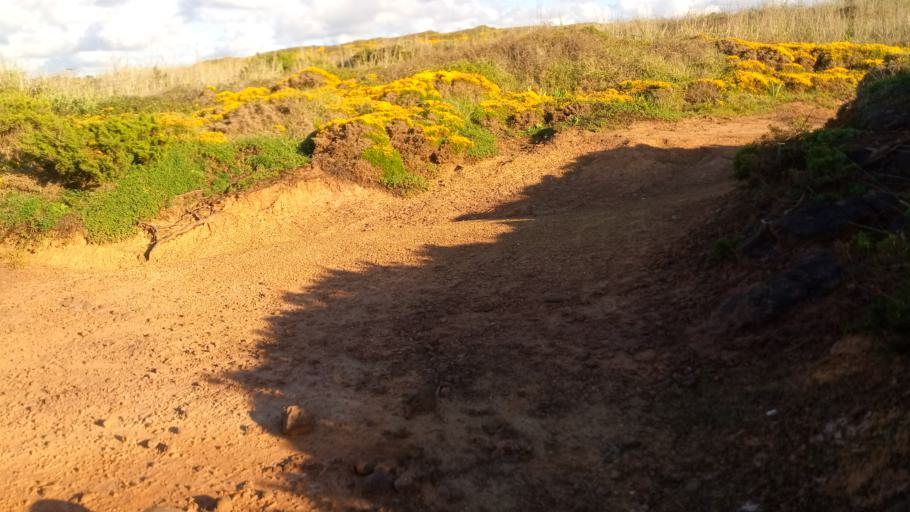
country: PT
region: Leiria
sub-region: Caldas da Rainha
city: Caldas da Rainha
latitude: 39.5064
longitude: -9.1559
